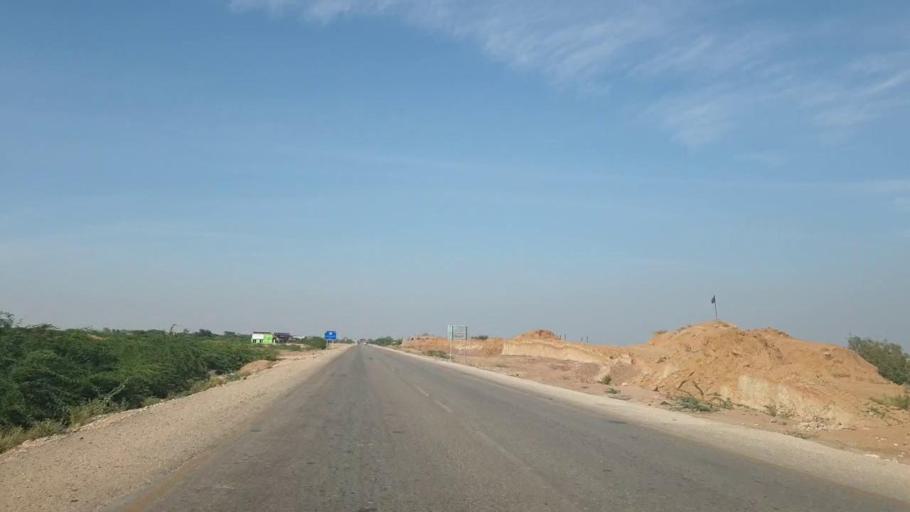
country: PK
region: Sindh
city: Sehwan
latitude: 26.3737
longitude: 67.8737
